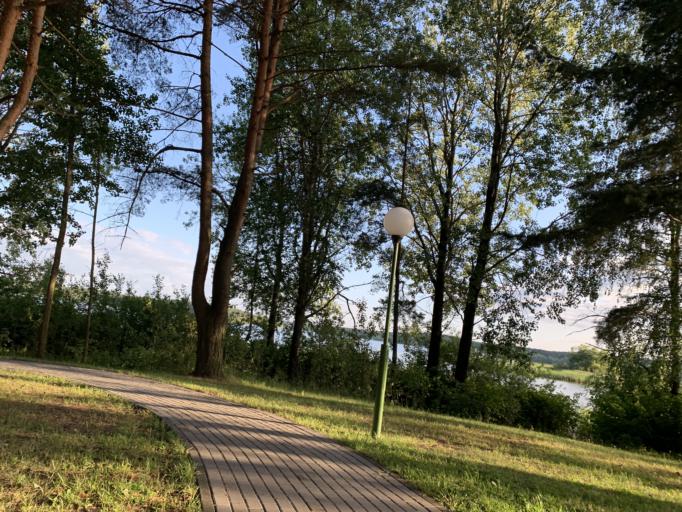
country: BY
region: Minsk
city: Khatsyezhyna
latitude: 53.9730
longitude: 27.3419
